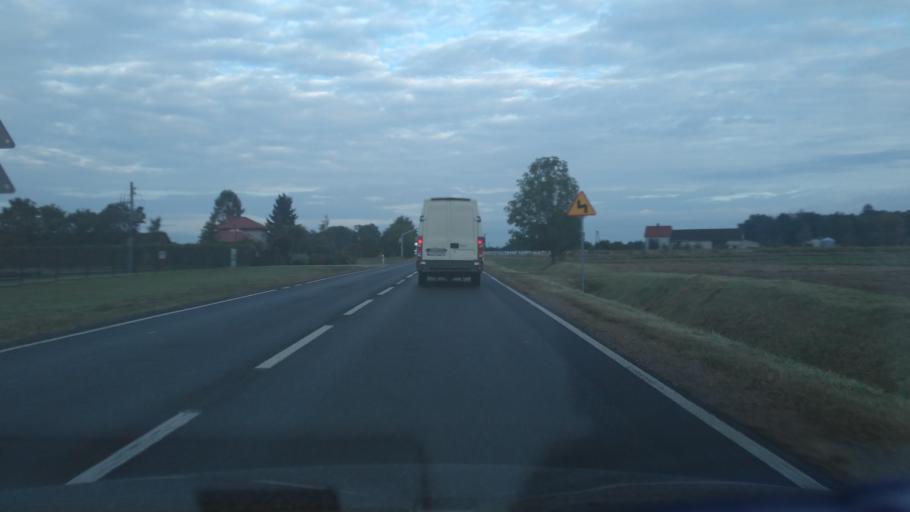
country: PL
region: Lublin Voivodeship
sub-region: Powiat leczynski
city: Spiczyn
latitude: 51.2975
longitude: 22.7734
